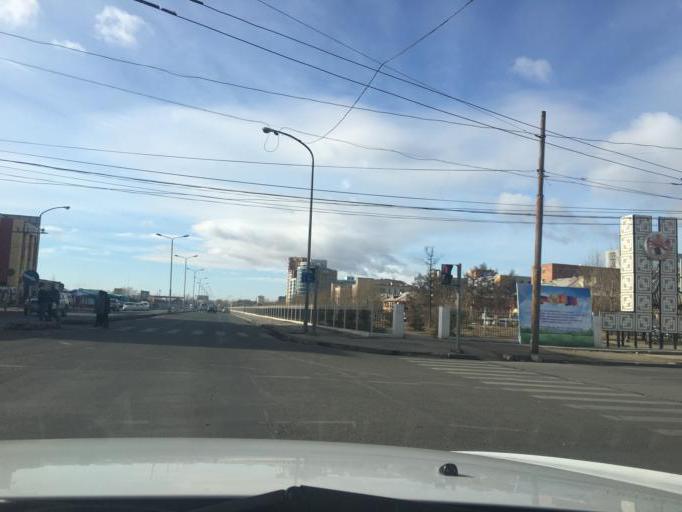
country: MN
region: Ulaanbaatar
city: Ulaanbaatar
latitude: 47.9092
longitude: 106.8836
